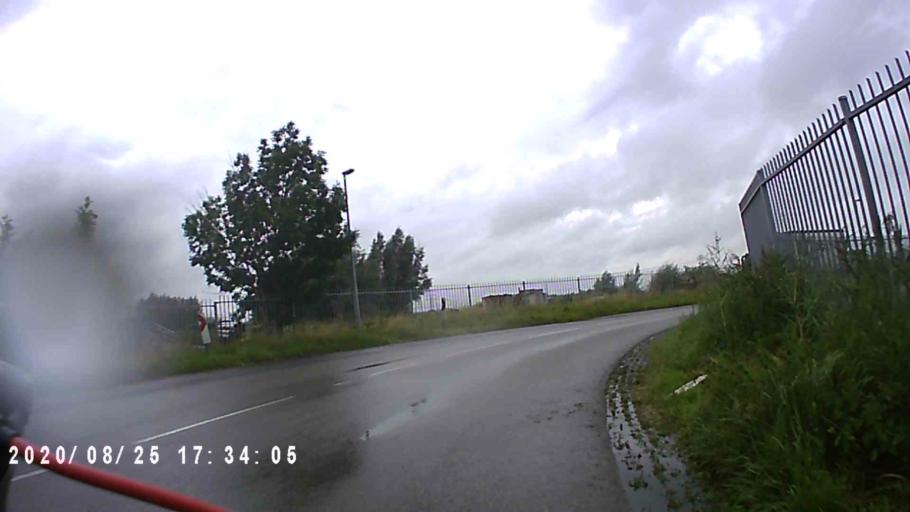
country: NL
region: Groningen
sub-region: Gemeente Zuidhorn
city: Aduard
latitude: 53.2158
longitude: 6.4860
